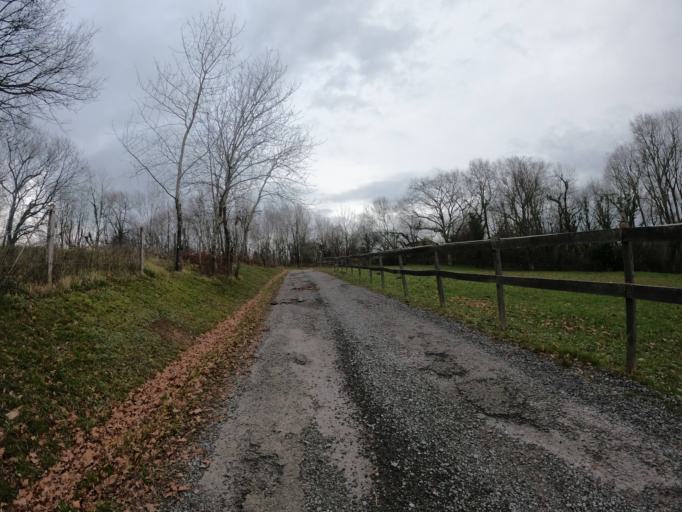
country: FR
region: Aquitaine
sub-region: Departement des Pyrenees-Atlantiques
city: Mazeres-Lezons
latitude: 43.2691
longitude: -0.3552
